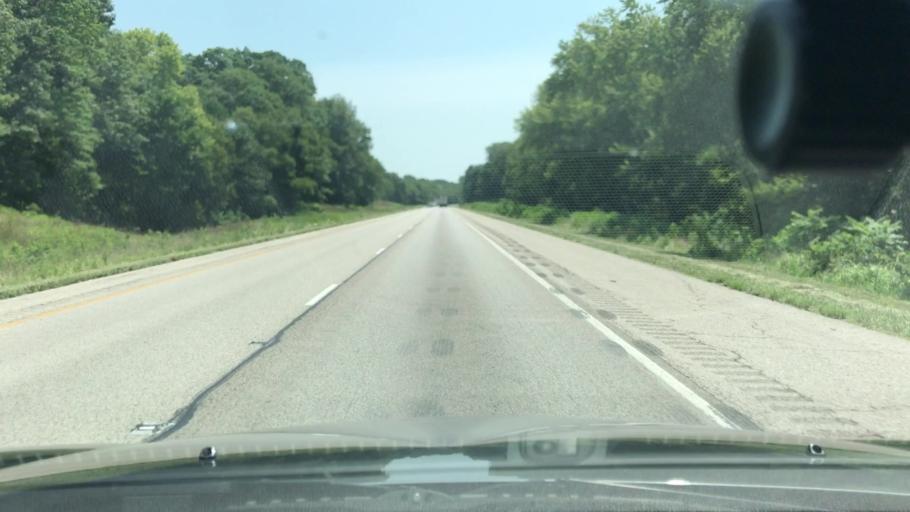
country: US
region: Illinois
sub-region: Washington County
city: Nashville
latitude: 38.4090
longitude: -89.4197
